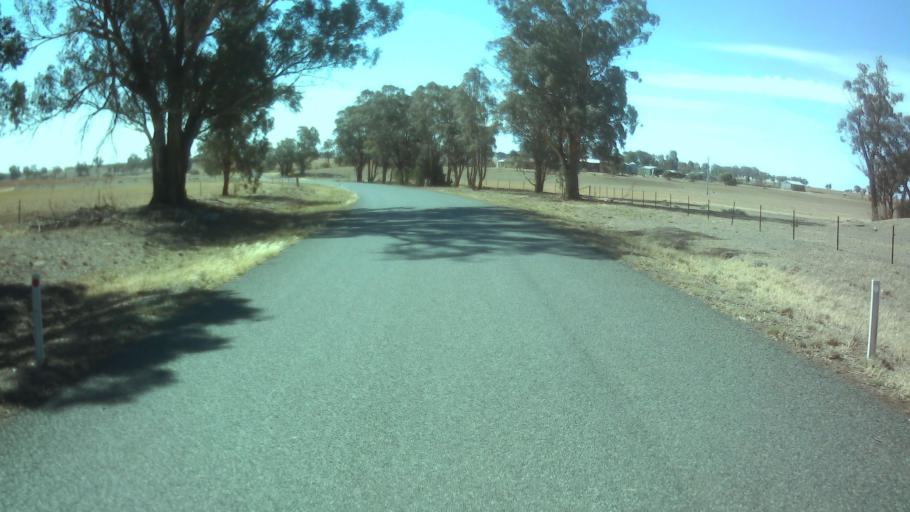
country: AU
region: New South Wales
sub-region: Weddin
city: Grenfell
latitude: -33.7645
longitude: 147.8640
